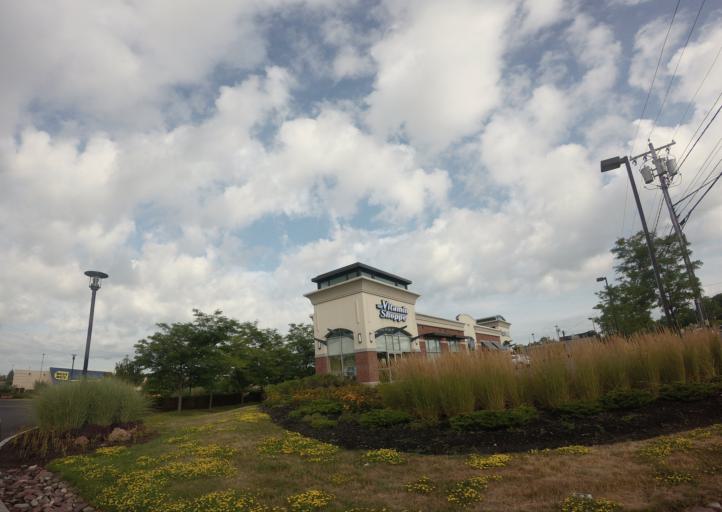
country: US
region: New York
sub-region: Onondaga County
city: East Syracuse
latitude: 43.0472
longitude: -76.0695
